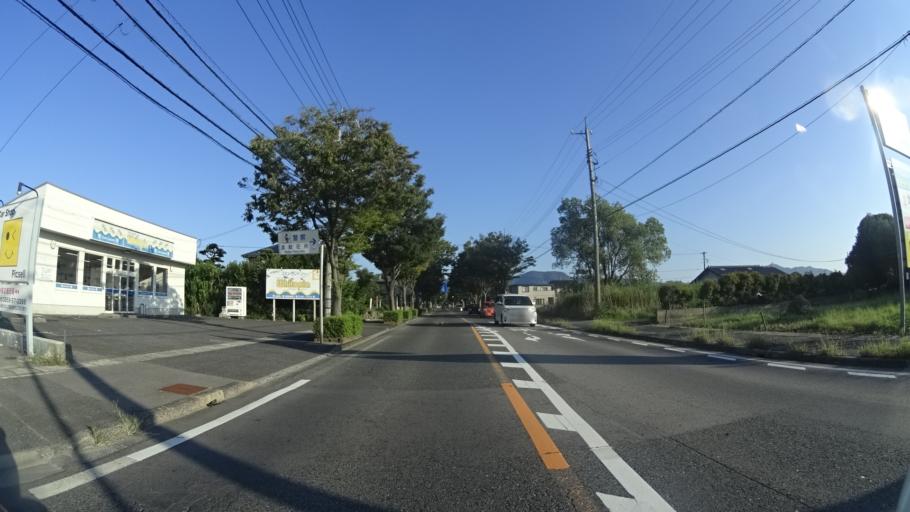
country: JP
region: Shimane
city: Sakaiminato
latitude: 35.5192
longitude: 133.2147
